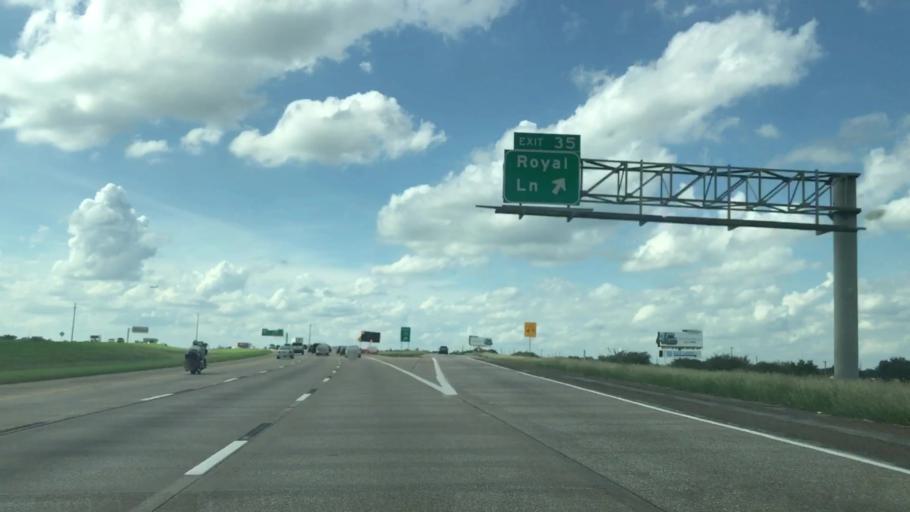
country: US
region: Texas
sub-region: Dallas County
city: Coppell
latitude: 32.9441
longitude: -97.0175
